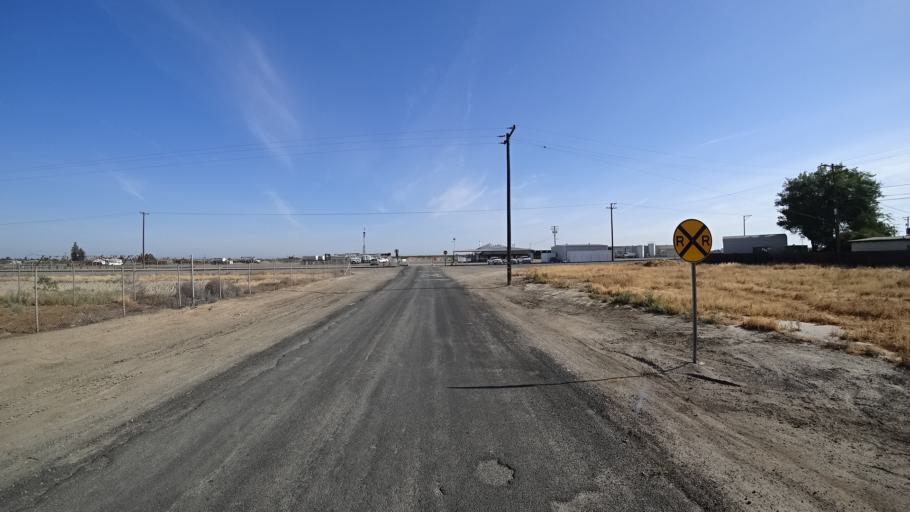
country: US
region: California
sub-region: Kings County
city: Hanford
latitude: 36.3296
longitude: -119.6127
